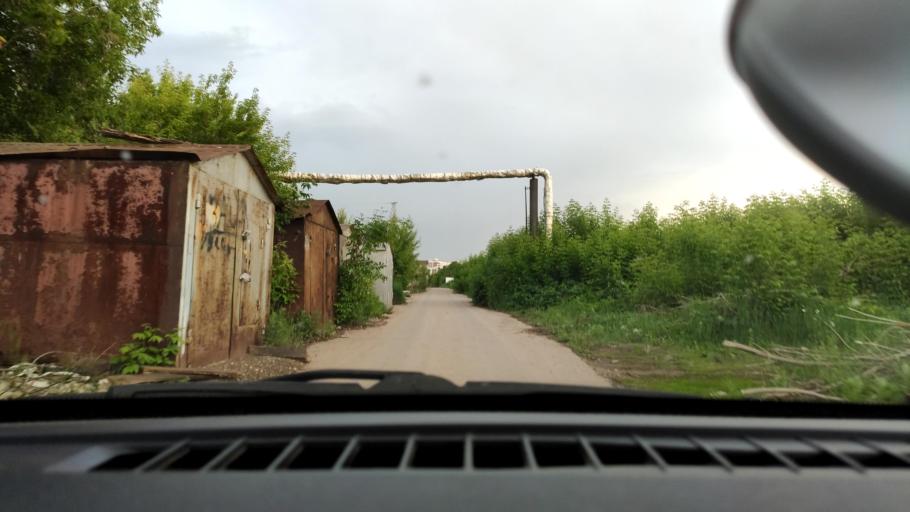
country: RU
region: Samara
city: Samara
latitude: 53.2516
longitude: 50.1821
